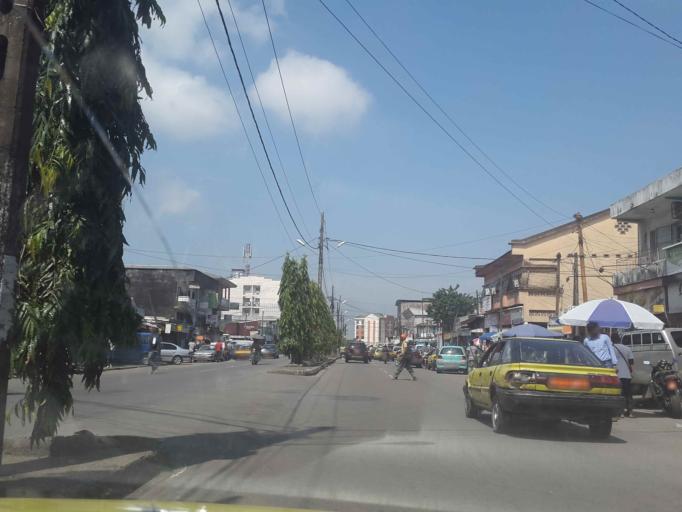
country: CM
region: Littoral
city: Douala
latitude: 4.0455
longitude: 9.6982
